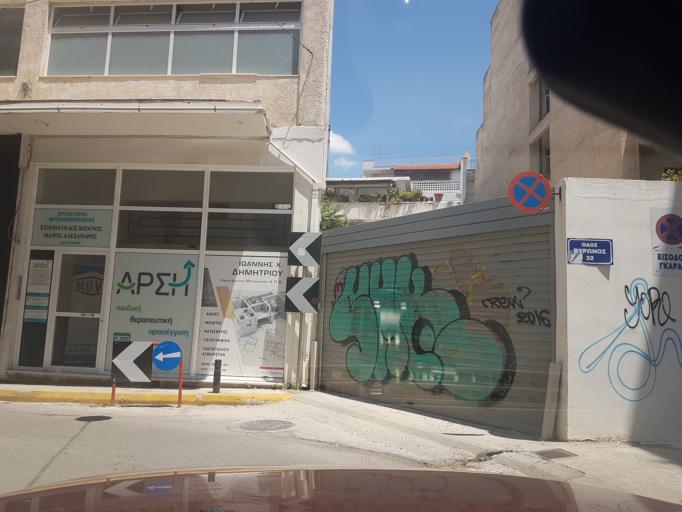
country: GR
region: Central Greece
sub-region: Nomos Evvoias
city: Chalkida
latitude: 38.4665
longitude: 23.5973
